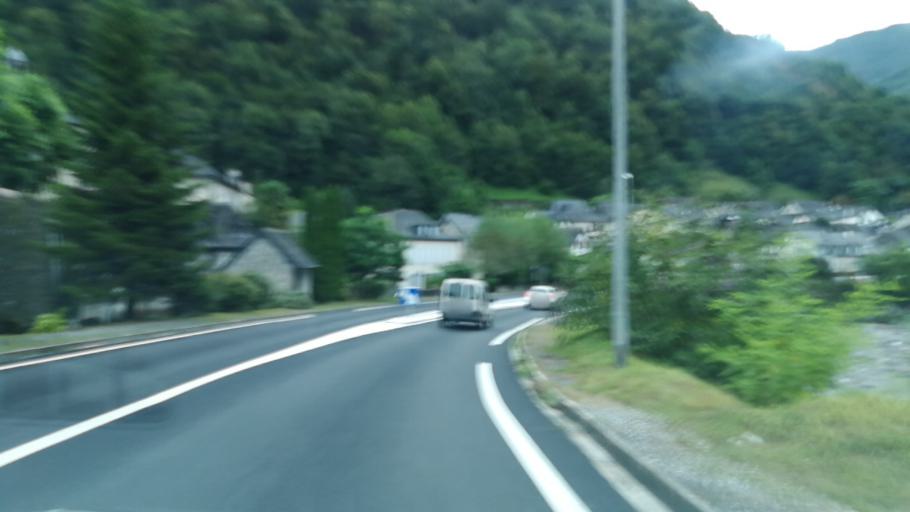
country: FR
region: Aquitaine
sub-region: Departement des Pyrenees-Atlantiques
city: Arette
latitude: 43.0507
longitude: -0.6012
